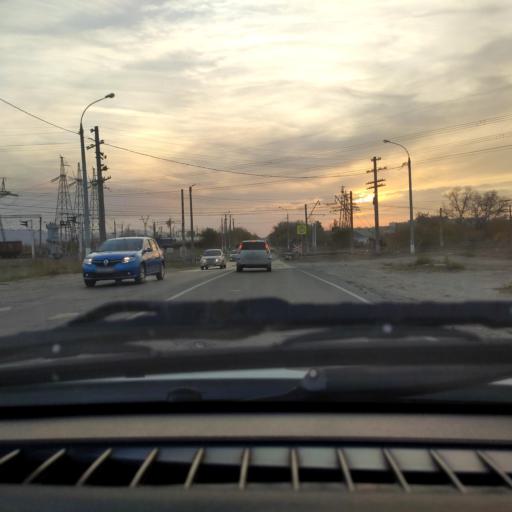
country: RU
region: Samara
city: Zhigulevsk
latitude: 53.4833
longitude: 49.5070
